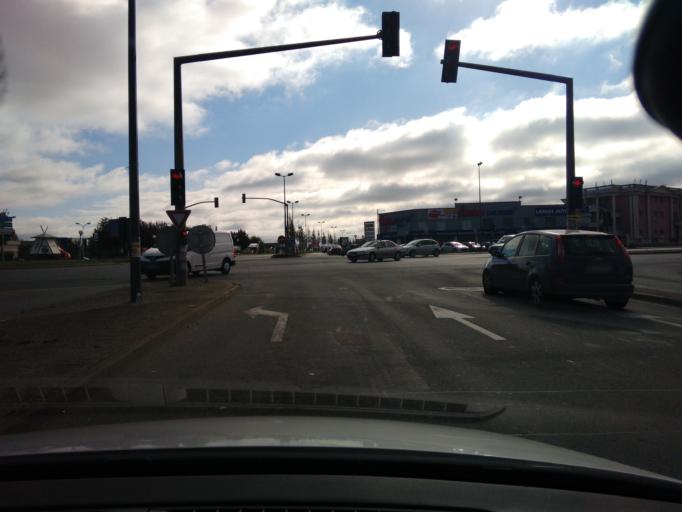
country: FR
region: Ile-de-France
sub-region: Departement de l'Essonne
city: Chilly-Mazarin
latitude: 48.7154
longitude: 2.2979
